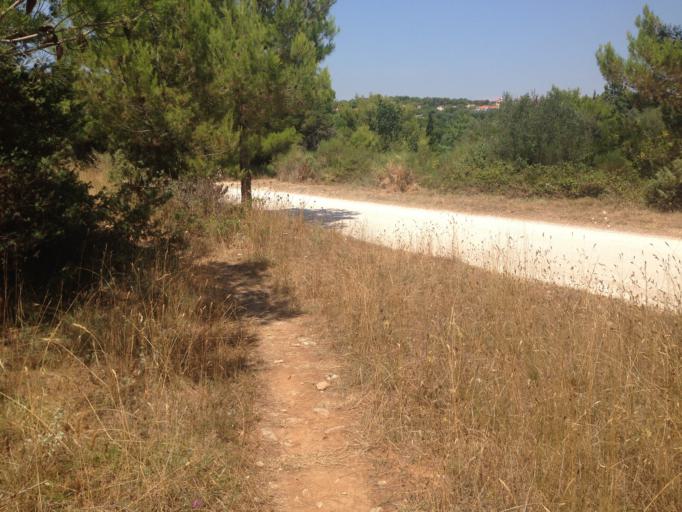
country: HR
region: Istarska
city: Medulin
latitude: 44.7967
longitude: 13.9075
